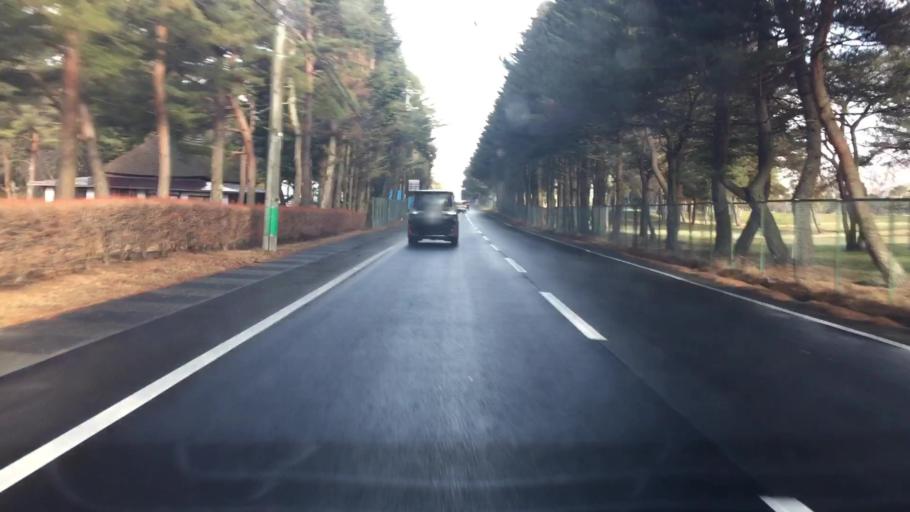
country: JP
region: Nagano
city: Saku
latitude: 36.3037
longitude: 138.6320
